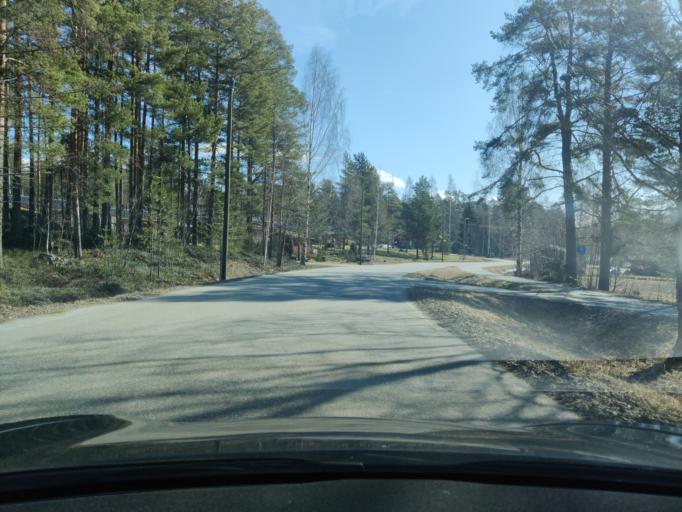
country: FI
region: Northern Savo
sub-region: Kuopio
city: Vehmersalmi
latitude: 62.7666
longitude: 28.0151
